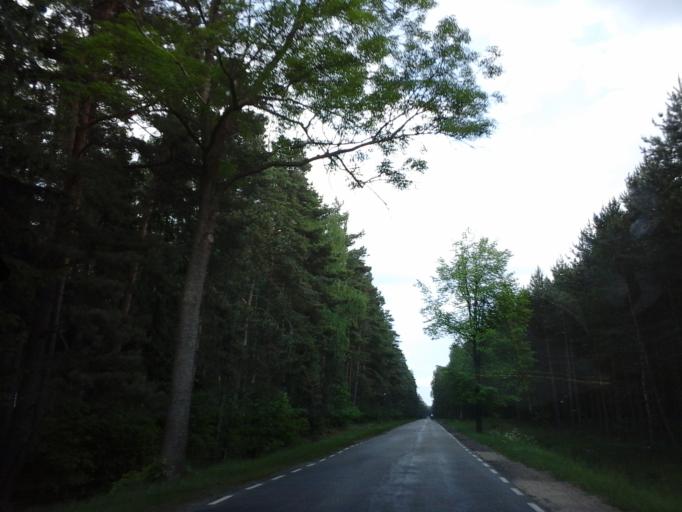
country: PL
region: West Pomeranian Voivodeship
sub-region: Powiat choszczenski
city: Drawno
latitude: 53.2410
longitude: 15.8192
